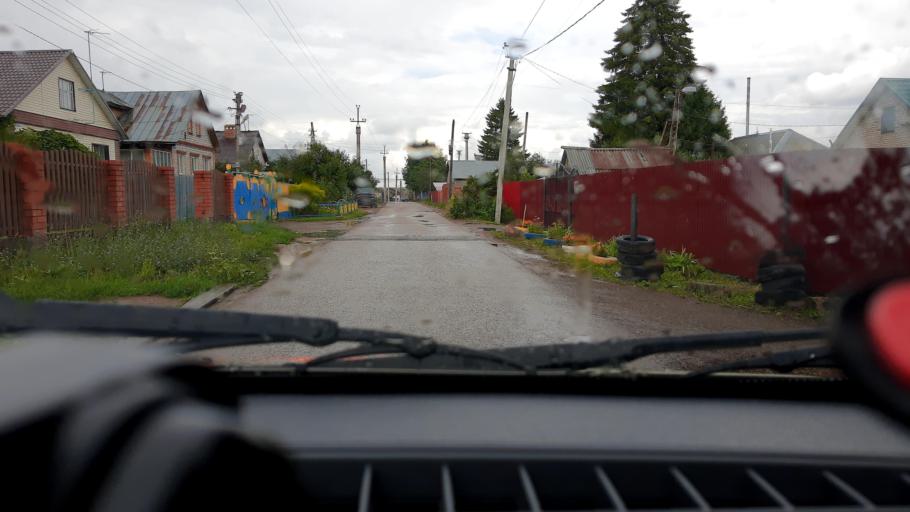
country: RU
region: Bashkortostan
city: Mikhaylovka
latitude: 54.8045
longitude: 55.7935
